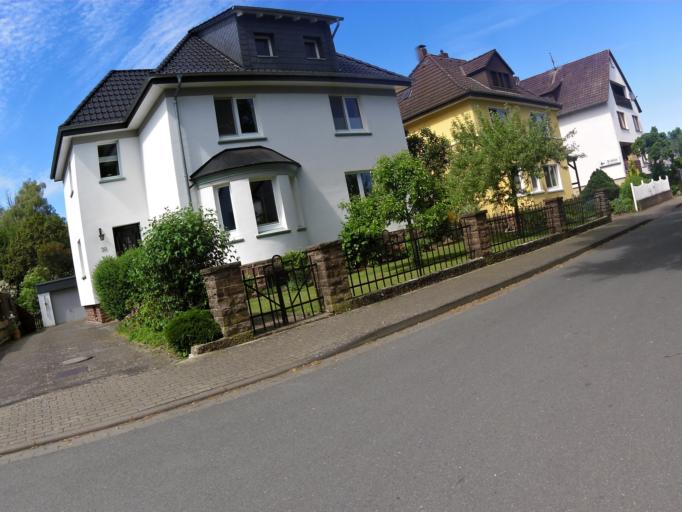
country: DE
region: North Rhine-Westphalia
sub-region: Regierungsbezirk Detmold
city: Hoexter
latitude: 51.7834
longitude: 9.3864
